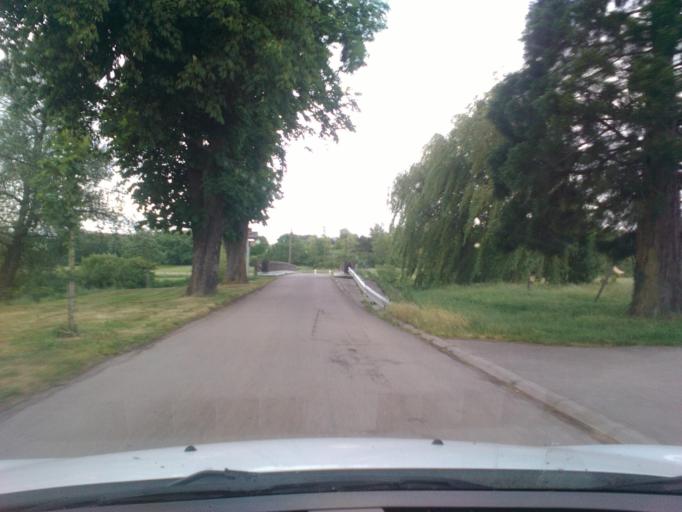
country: FR
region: Lorraine
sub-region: Departement de Meurthe-et-Moselle
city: Gerbeviller
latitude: 48.4636
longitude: 6.5511
